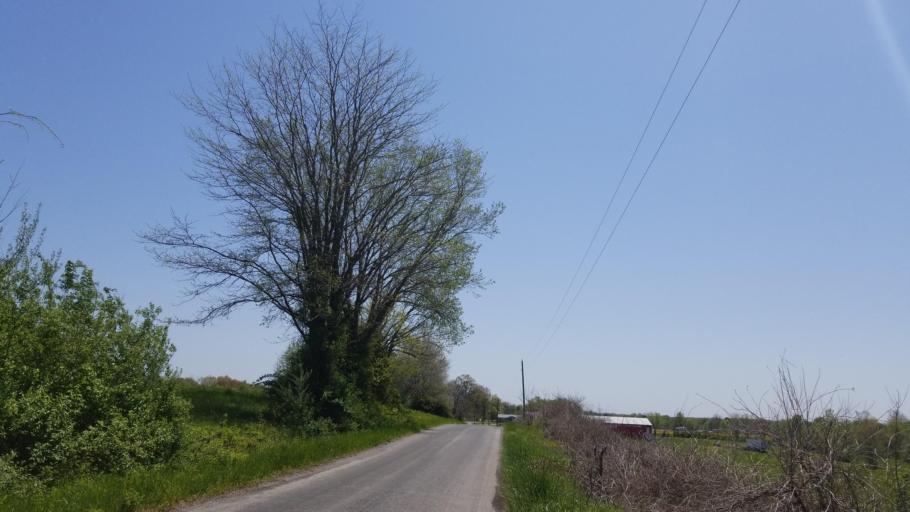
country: US
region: Illinois
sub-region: Saline County
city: Harrisburg
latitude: 37.8504
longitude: -88.6010
